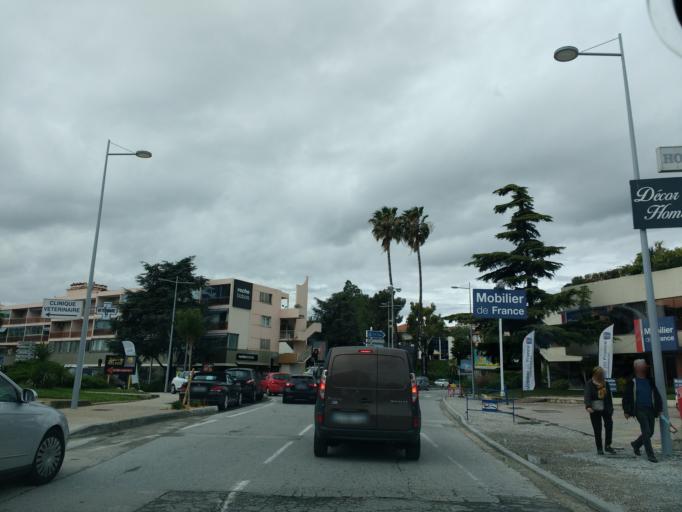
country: FR
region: Provence-Alpes-Cote d'Azur
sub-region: Departement des Alpes-Maritimes
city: Saint-Laurent-du-Var
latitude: 43.6596
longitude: 7.1936
